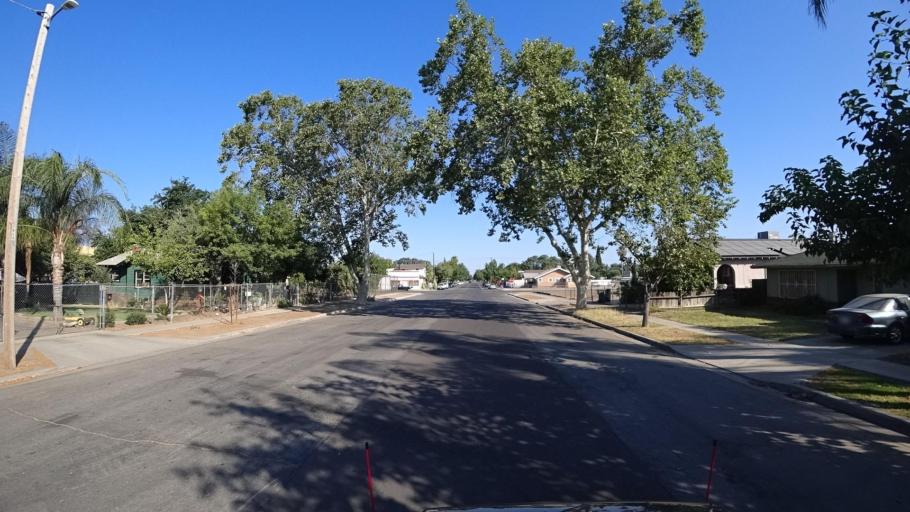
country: US
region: California
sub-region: Fresno County
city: Fresno
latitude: 36.7263
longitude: -119.7994
